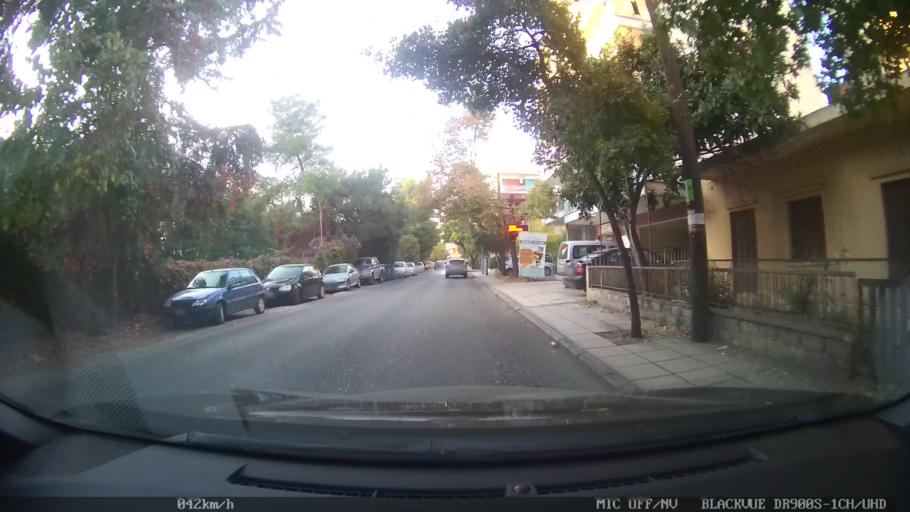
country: GR
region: Central Macedonia
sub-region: Nomos Thessalonikis
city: Triandria
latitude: 40.6100
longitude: 22.9810
